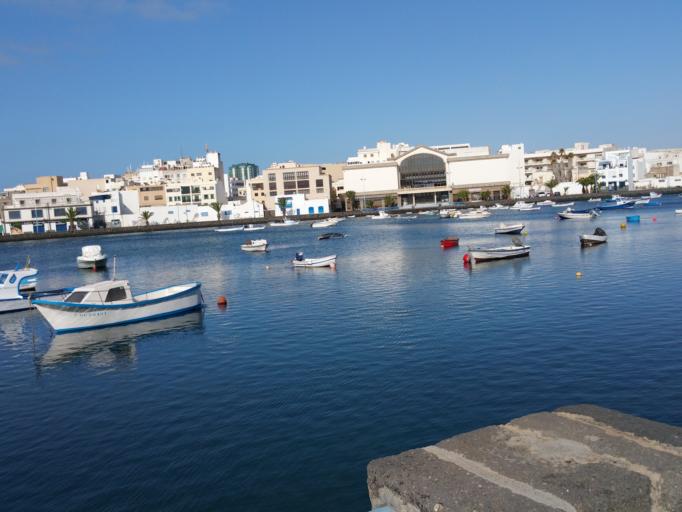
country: ES
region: Canary Islands
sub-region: Provincia de Las Palmas
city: Arrecife
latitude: 28.9618
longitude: -13.5461
